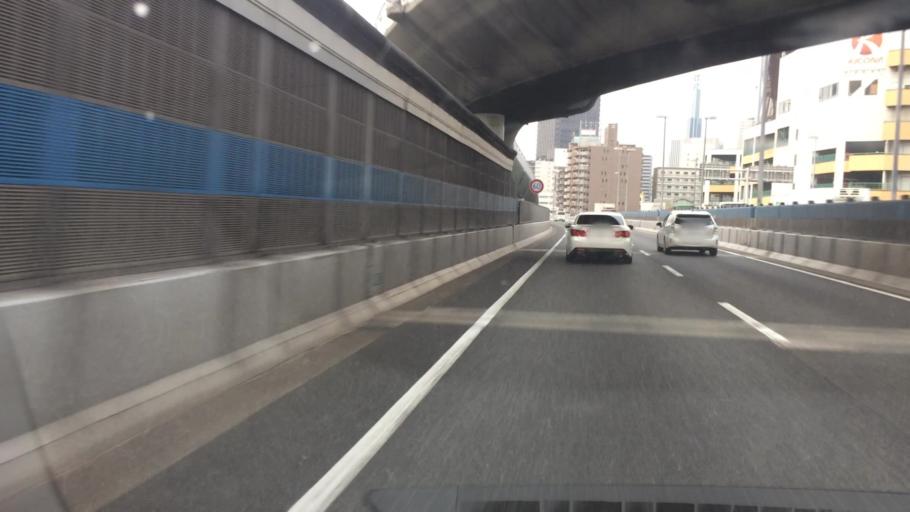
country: JP
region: Hyogo
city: Kobe
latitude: 34.6934
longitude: 135.2038
